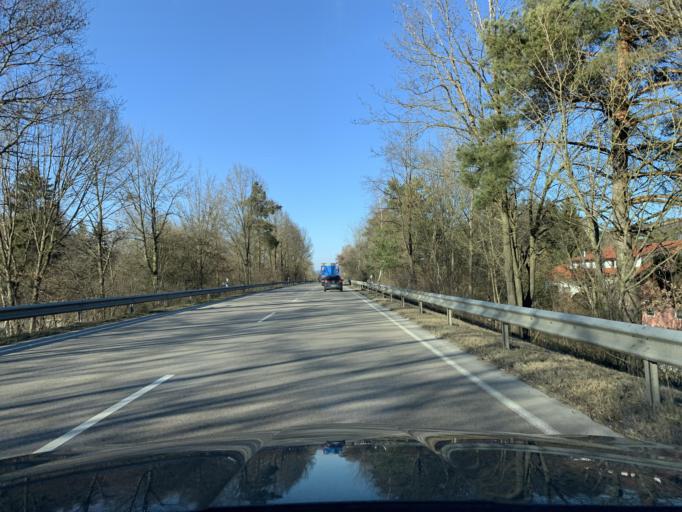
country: DE
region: Bavaria
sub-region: Upper Palatinate
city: Pemfling
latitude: 49.3032
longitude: 12.6296
